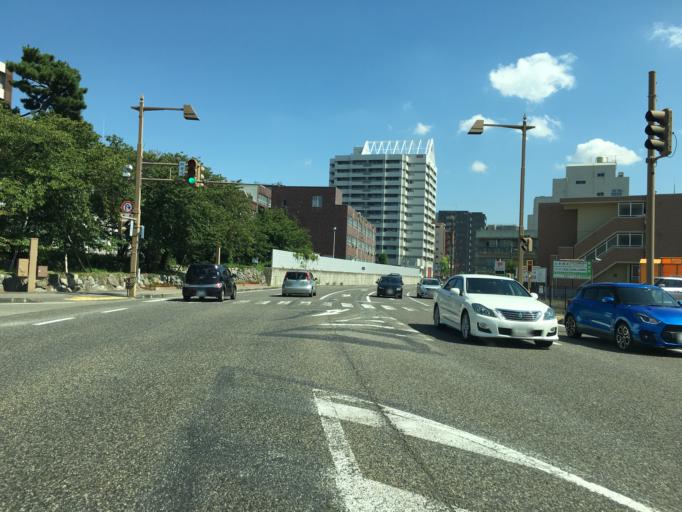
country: JP
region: Niigata
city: Niigata-shi
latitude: 37.9174
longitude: 139.0344
